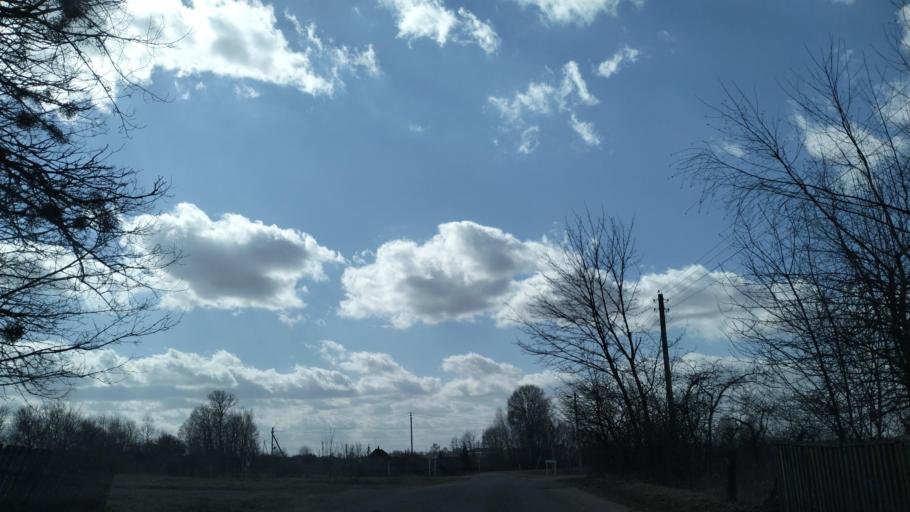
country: BY
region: Grodnenskaya
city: Karelichy
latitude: 53.6615
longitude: 26.1294
